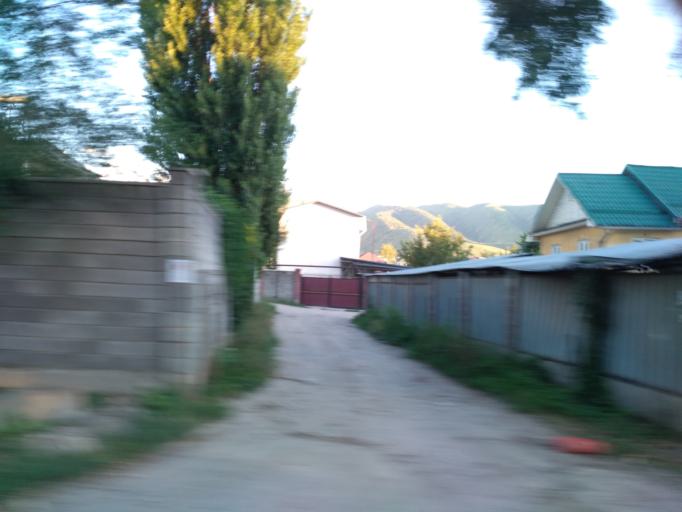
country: KZ
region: Almaty Qalasy
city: Almaty
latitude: 43.1778
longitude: 76.7513
